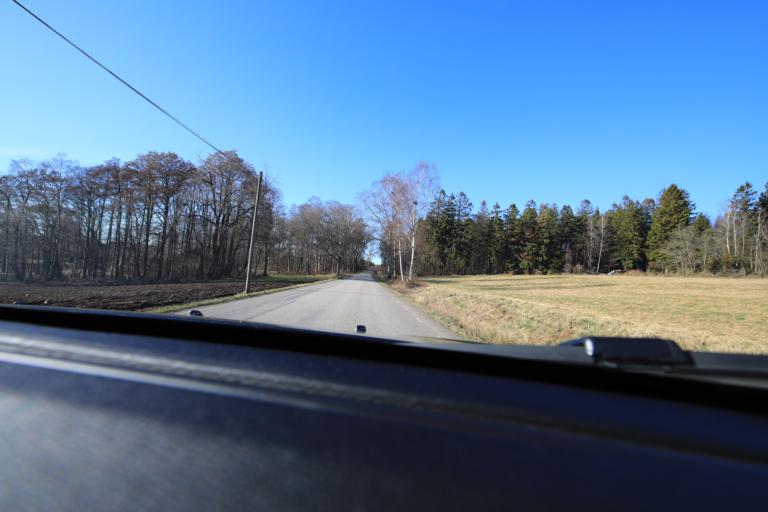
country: SE
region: Halland
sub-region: Varbergs Kommun
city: Tvaaker
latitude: 57.0629
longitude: 12.4238
